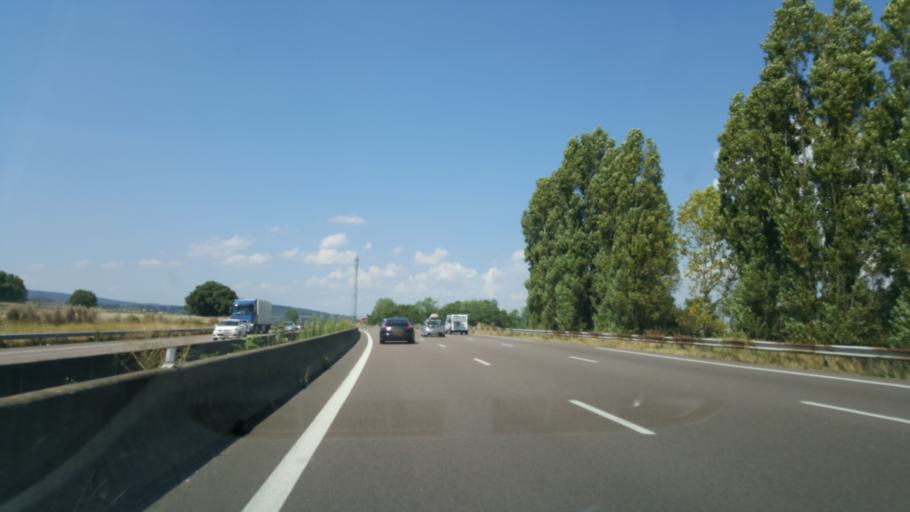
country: FR
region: Bourgogne
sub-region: Departement de Saone-et-Loire
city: Tournus
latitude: 46.5407
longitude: 4.9190
